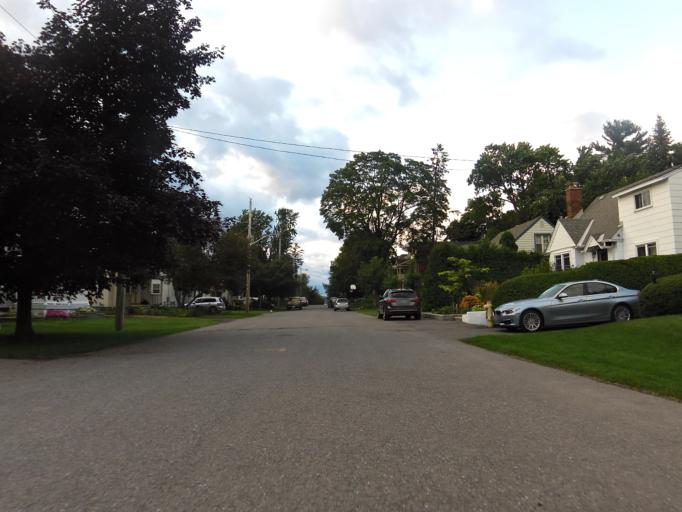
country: CA
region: Ontario
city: Ottawa
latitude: 45.3899
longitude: -75.7488
